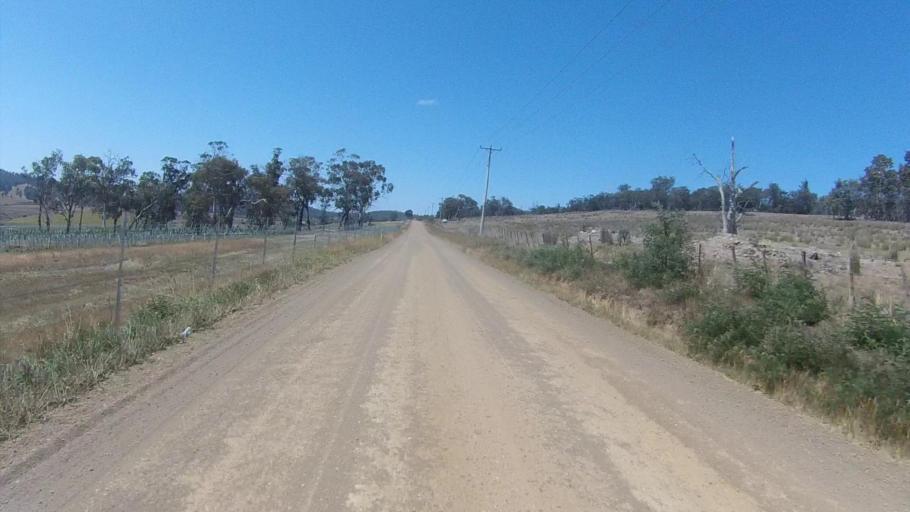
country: AU
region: Tasmania
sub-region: Sorell
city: Sorell
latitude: -42.8194
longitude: 147.6319
